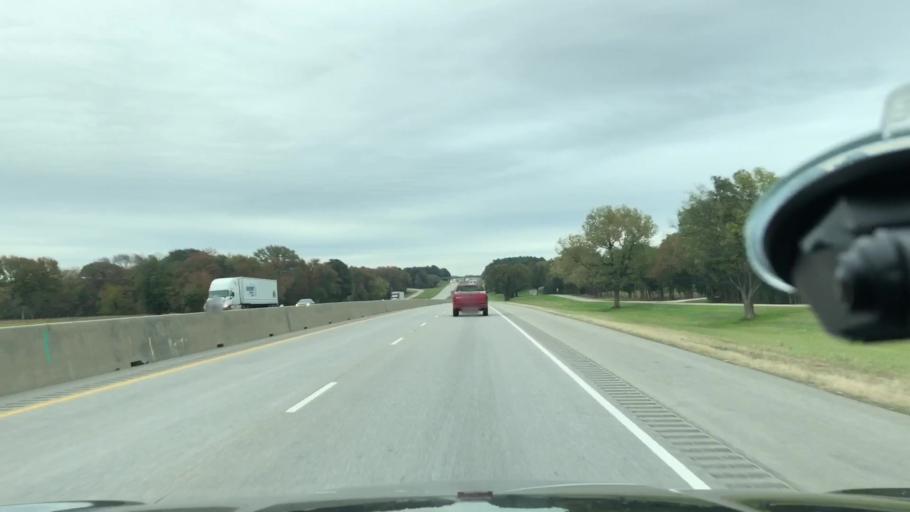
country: US
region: Texas
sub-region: Franklin County
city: Mount Vernon
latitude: 33.1615
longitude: -95.1440
